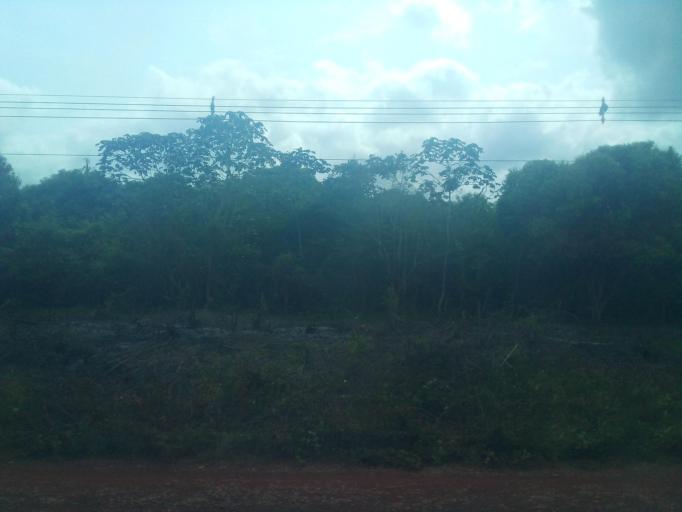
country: BR
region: Maranhao
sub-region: Icatu
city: Icatu
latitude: -2.9438
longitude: -44.3458
